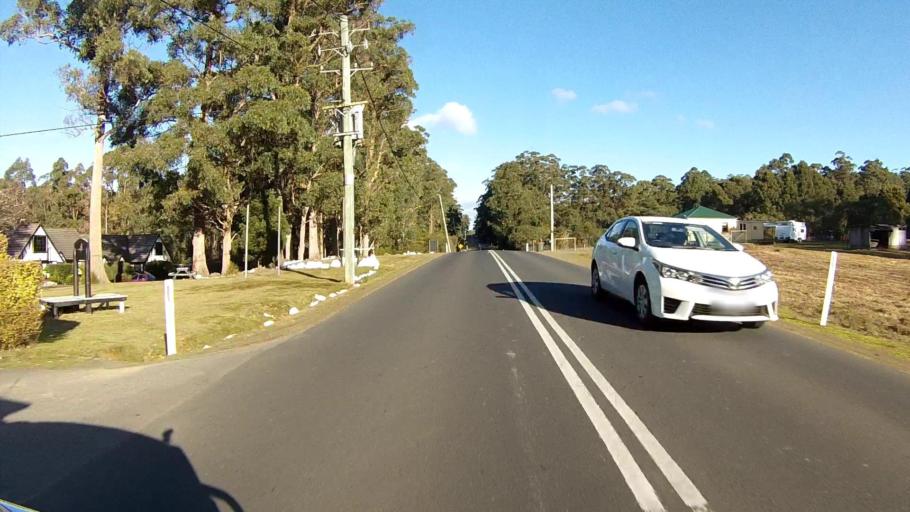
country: AU
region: Tasmania
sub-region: Clarence
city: Sandford
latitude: -43.1253
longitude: 147.8500
